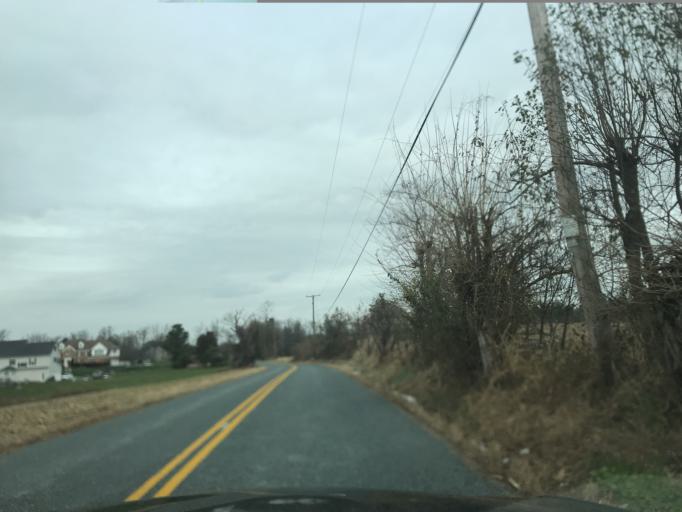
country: US
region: Maryland
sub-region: Harford County
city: Jarrettsville
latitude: 39.6705
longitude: -76.4313
